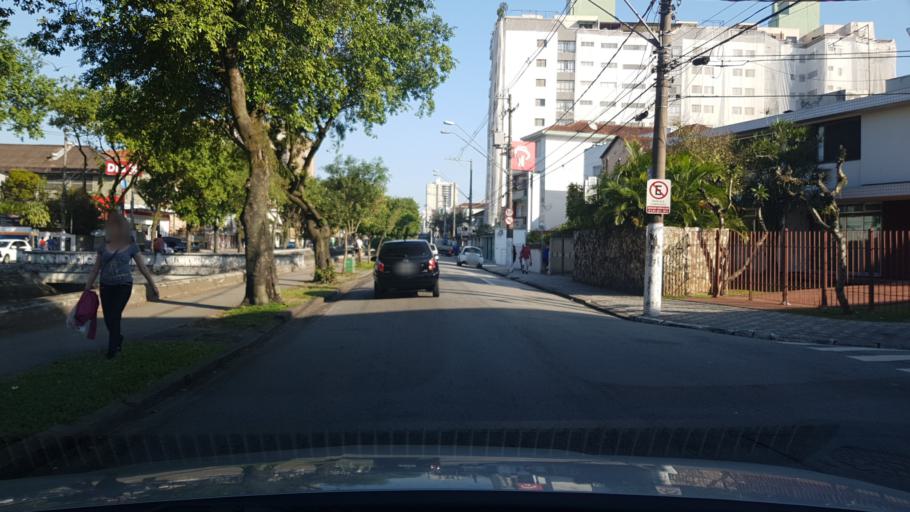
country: BR
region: Sao Paulo
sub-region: Santos
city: Santos
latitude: -23.9558
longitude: -46.3446
